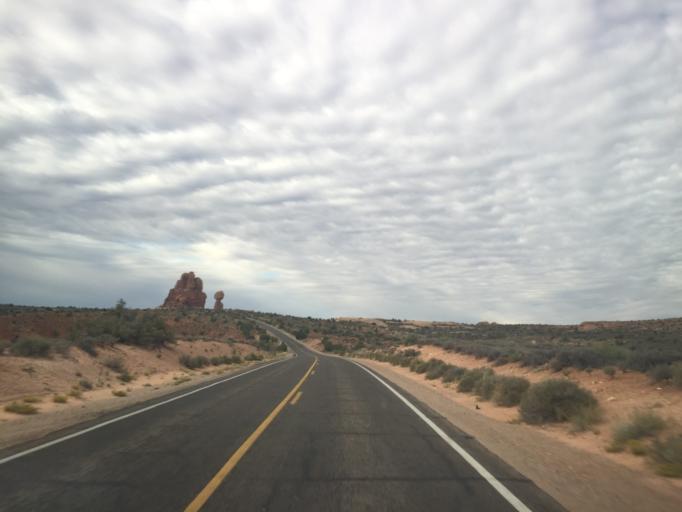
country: US
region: Utah
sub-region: Grand County
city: Moab
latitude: 38.7108
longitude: -109.5605
